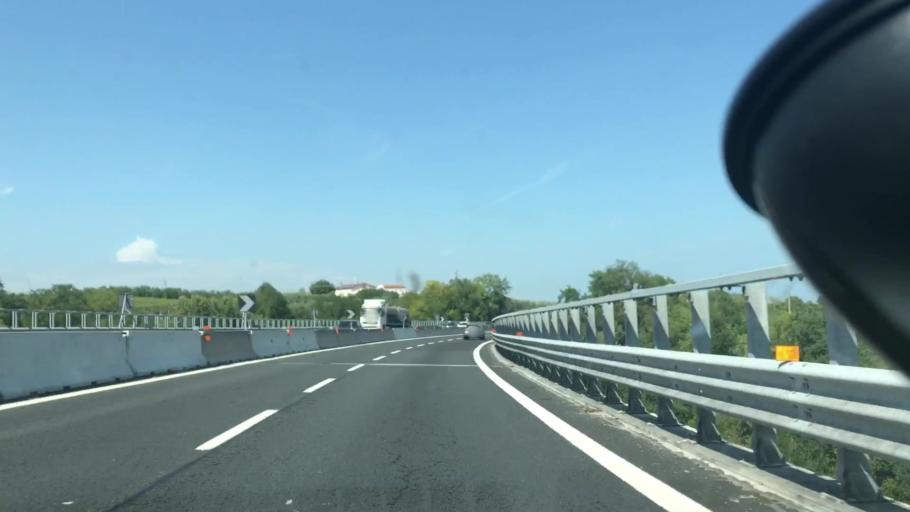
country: IT
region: Abruzzo
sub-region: Provincia di Chieti
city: Ortona
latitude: 42.3384
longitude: 14.3601
